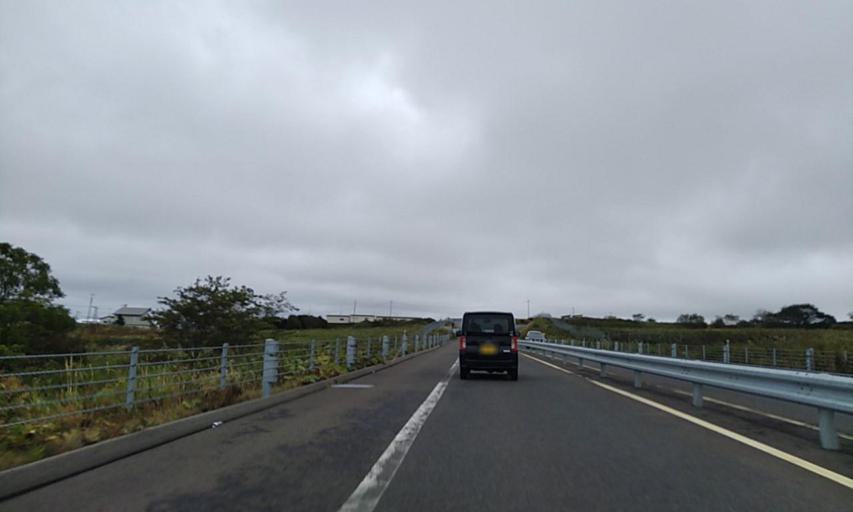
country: JP
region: Hokkaido
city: Nemuro
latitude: 43.3109
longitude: 145.5433
